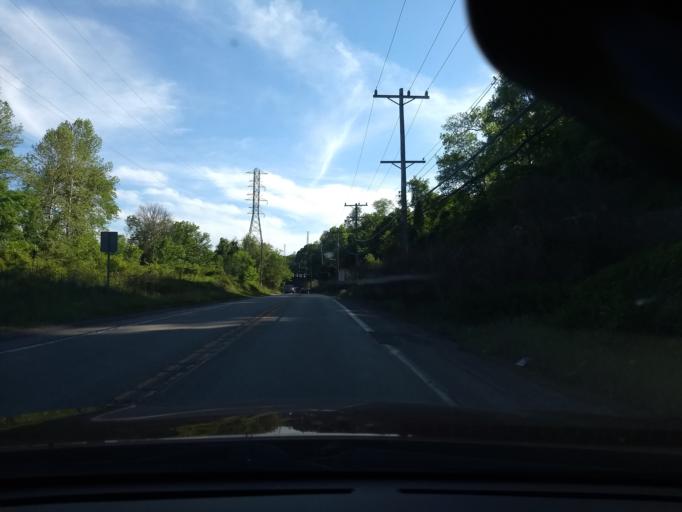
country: US
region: Pennsylvania
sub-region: Allegheny County
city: Dravosburg
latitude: 40.3393
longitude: -79.8943
